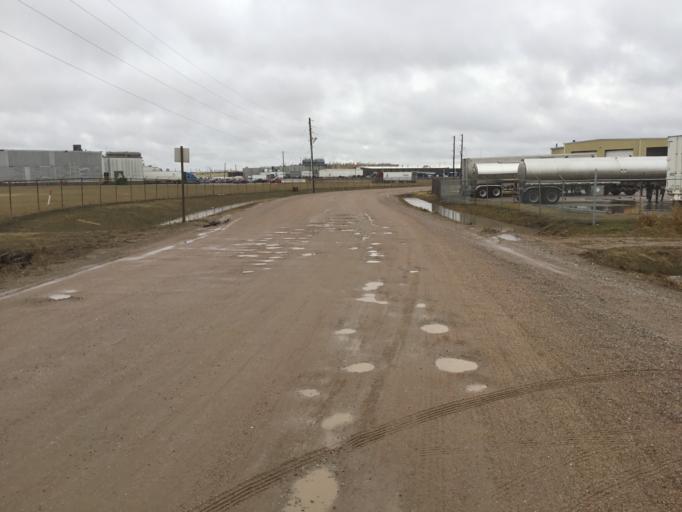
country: US
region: Kansas
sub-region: Sedgwick County
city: Wichita
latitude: 37.7300
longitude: -97.3287
